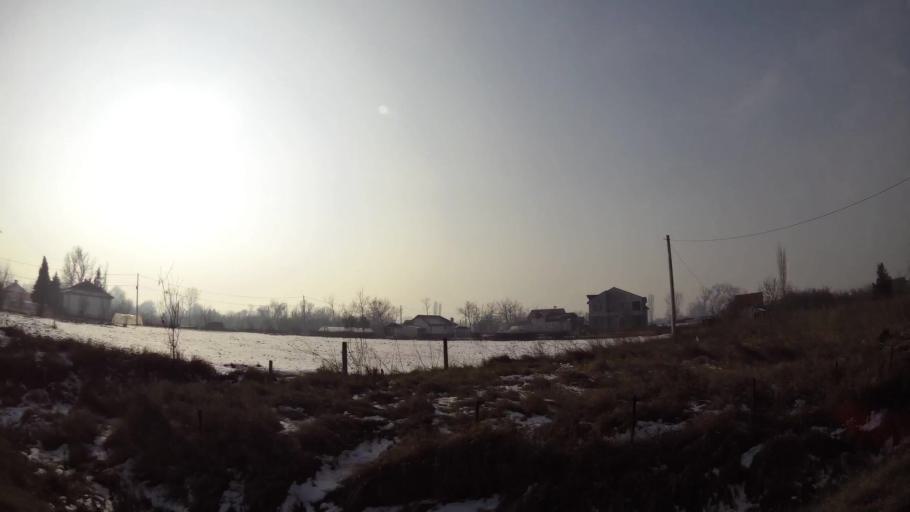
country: MK
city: Kadino
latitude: 41.9703
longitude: 21.5934
